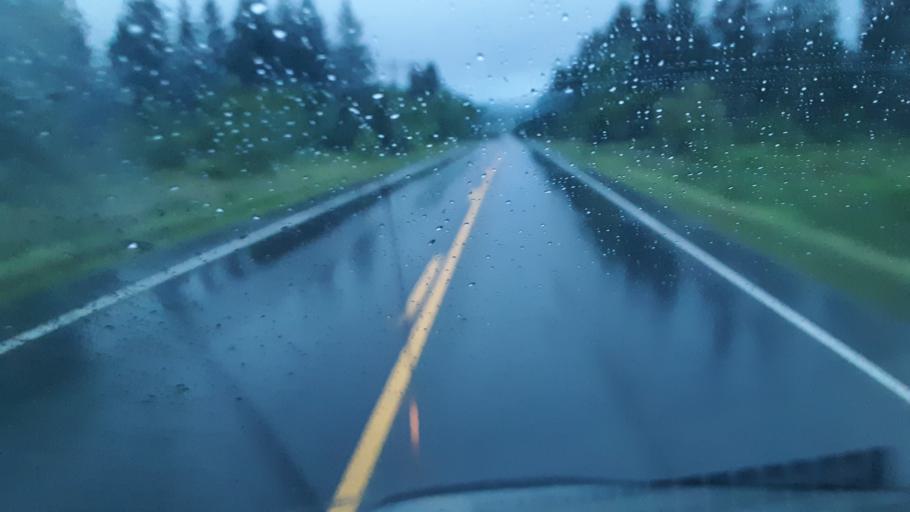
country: US
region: Maine
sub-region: Penobscot County
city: Patten
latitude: 45.9406
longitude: -68.4514
